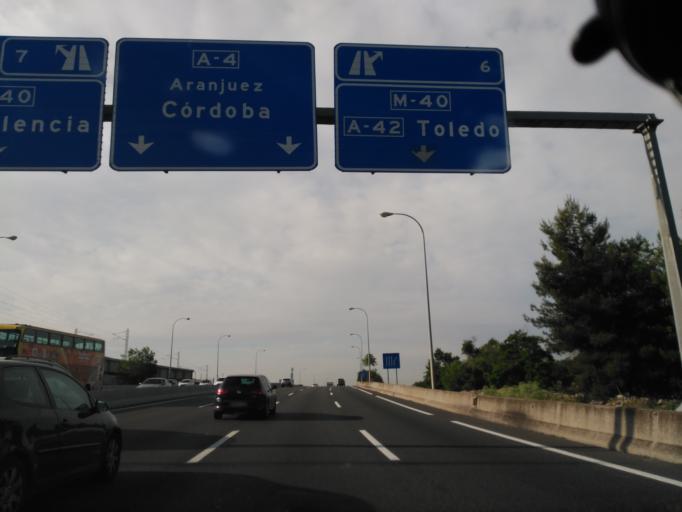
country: ES
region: Madrid
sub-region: Provincia de Madrid
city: Villaverde
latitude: 40.3686
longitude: -3.6787
